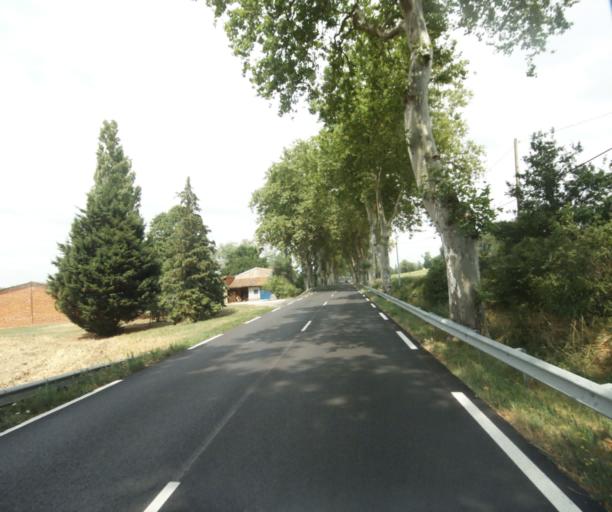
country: FR
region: Midi-Pyrenees
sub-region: Departement de la Haute-Garonne
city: Revel
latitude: 43.4406
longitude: 1.9521
